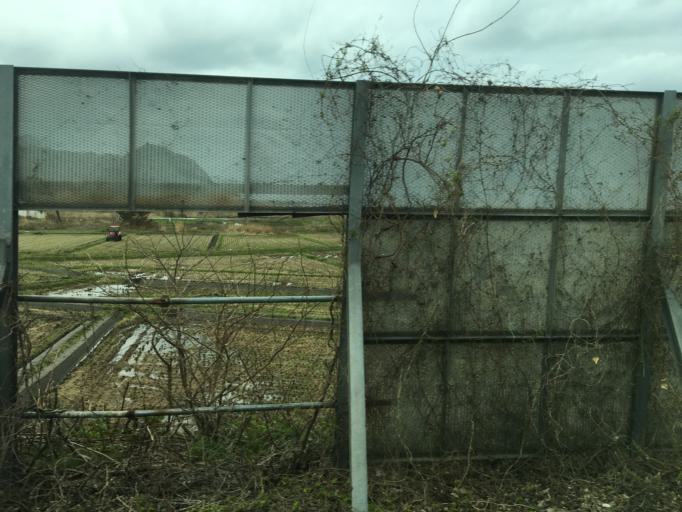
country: JP
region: Aomori
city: Shimokizukuri
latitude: 40.6861
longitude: 139.9704
